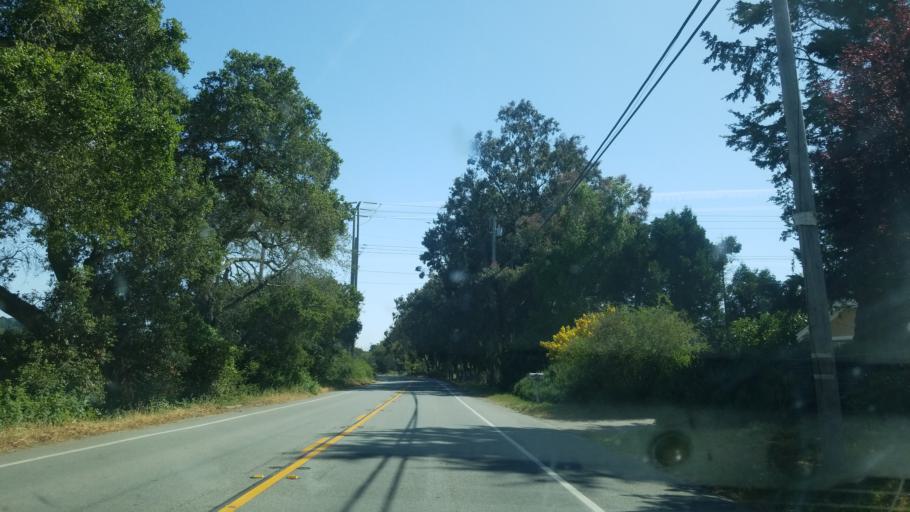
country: US
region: California
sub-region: Santa Cruz County
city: Soquel
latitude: 37.0123
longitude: -121.9529
